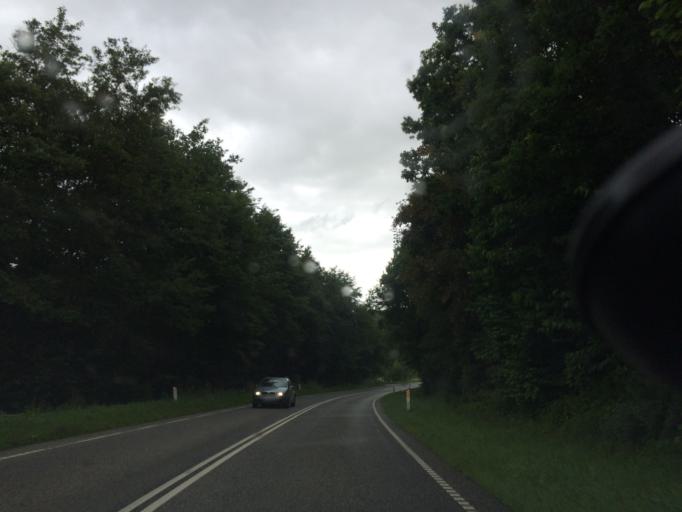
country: DK
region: Central Jutland
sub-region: Skanderborg Kommune
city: Ry
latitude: 56.1628
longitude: 9.8118
